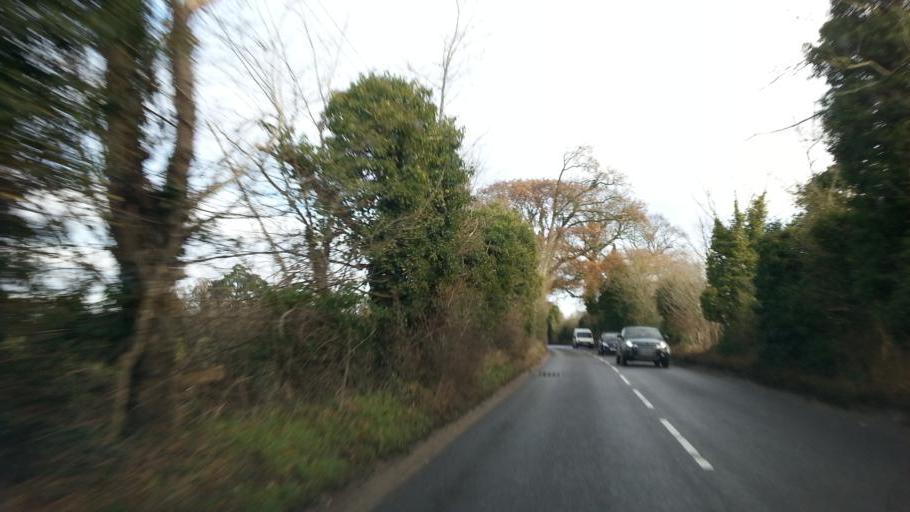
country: GB
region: England
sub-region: Suffolk
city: Wickham Market
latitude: 52.1128
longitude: 1.3780
